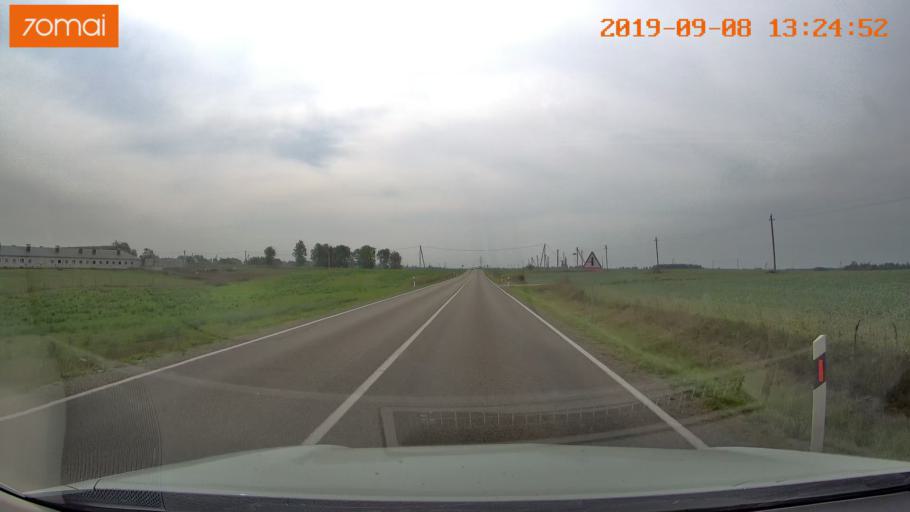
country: LT
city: Jieznas
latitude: 54.6192
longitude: 24.1694
